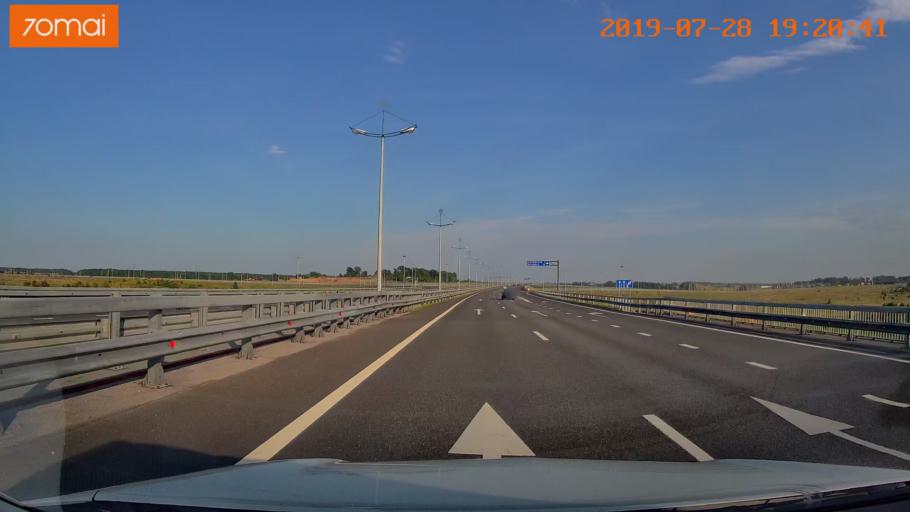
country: RU
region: Kaliningrad
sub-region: Zelenogradskiy Rayon
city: Zelenogradsk
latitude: 54.9130
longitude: 20.4920
